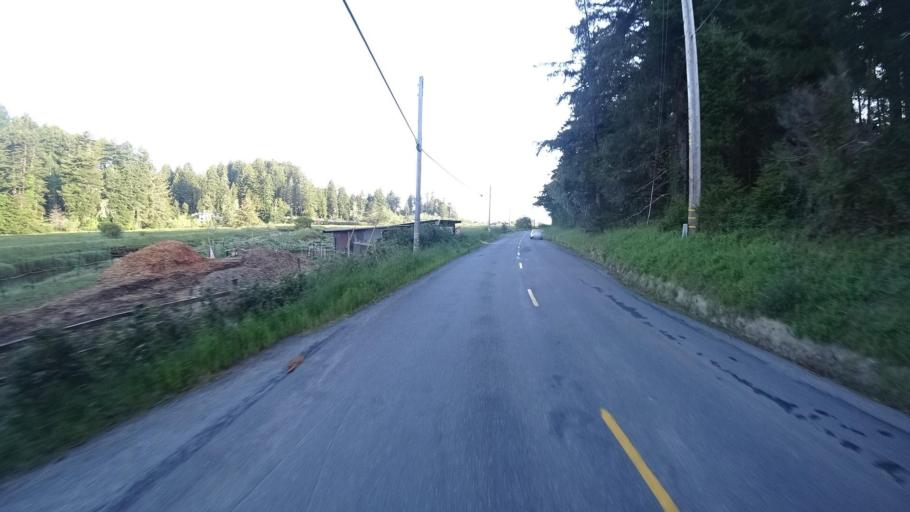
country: US
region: California
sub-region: Humboldt County
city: Myrtletown
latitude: 40.7826
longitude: -124.1187
